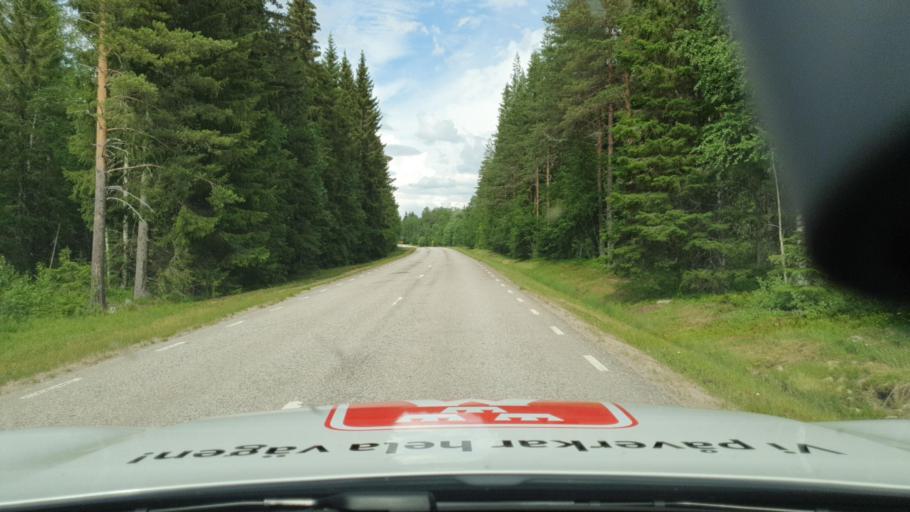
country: NO
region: Hedmark
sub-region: Trysil
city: Innbygda
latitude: 60.9651
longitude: 12.4822
